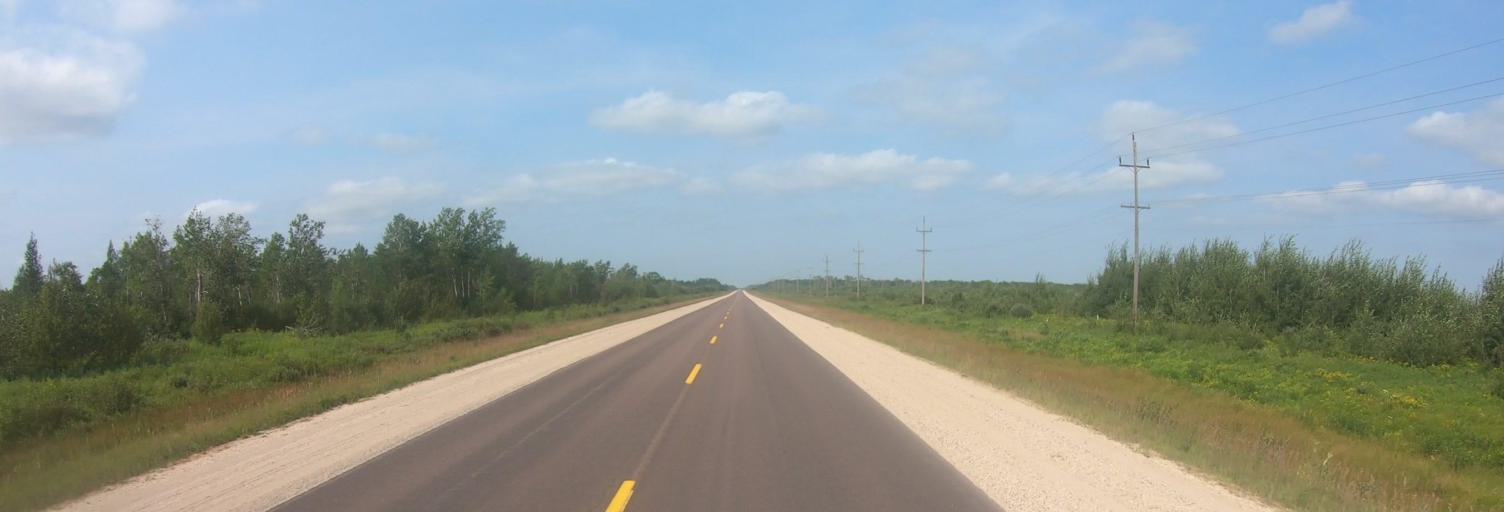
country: CA
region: Manitoba
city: La Broquerie
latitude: 49.2671
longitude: -96.3772
